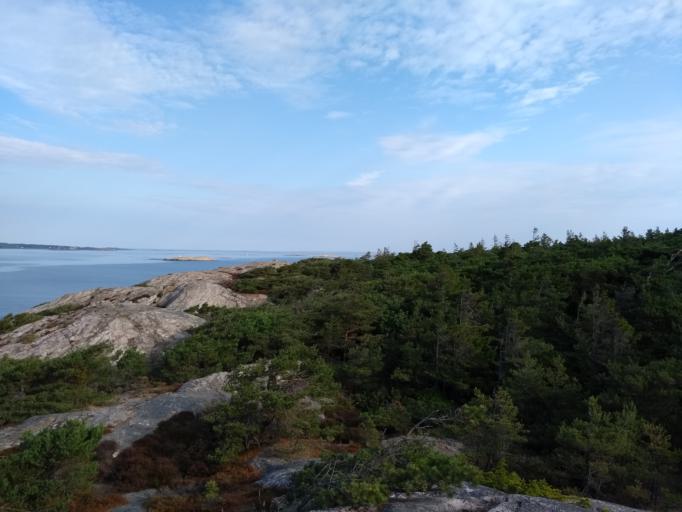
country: SE
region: Vaestra Goetaland
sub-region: Stromstads Kommun
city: Stroemstad
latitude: 58.8668
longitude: 11.1222
